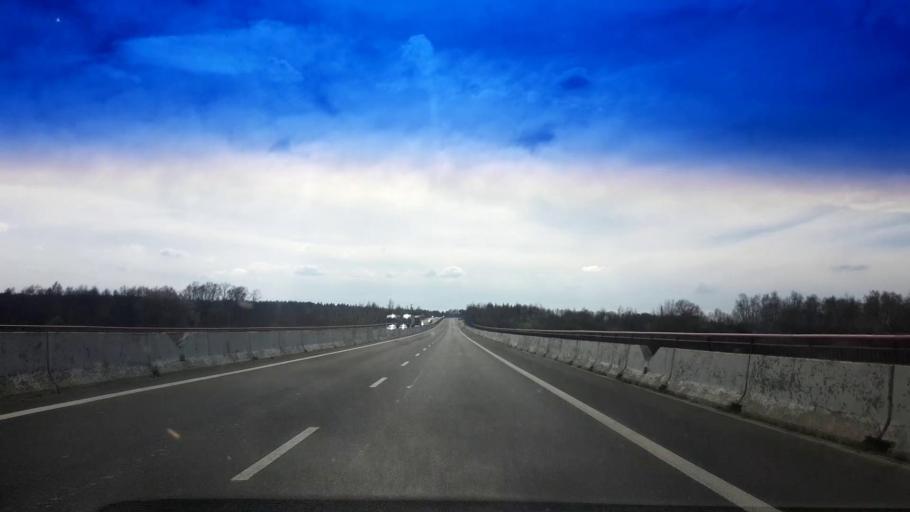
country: DE
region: Bavaria
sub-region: Upper Franconia
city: Schirnding
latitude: 50.0924
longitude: 12.2761
